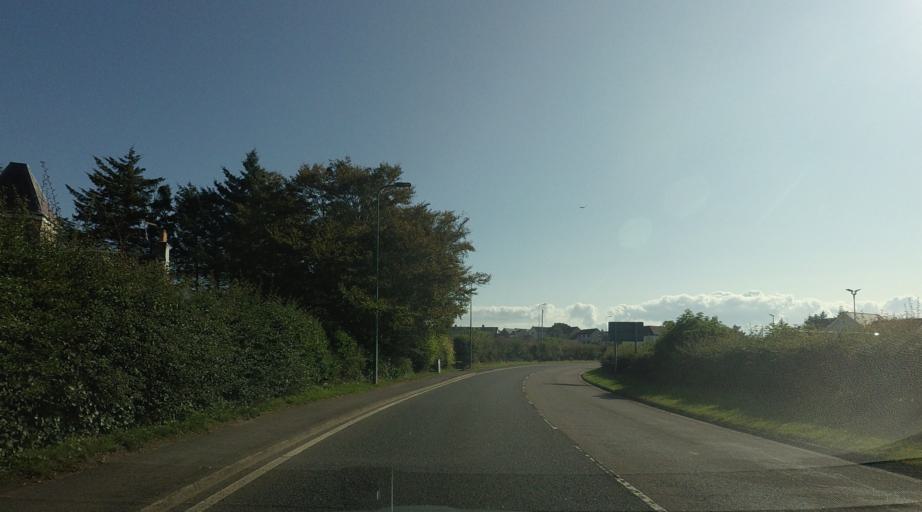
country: GB
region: Scotland
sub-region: Highland
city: Thurso
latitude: 58.5913
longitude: -3.5168
